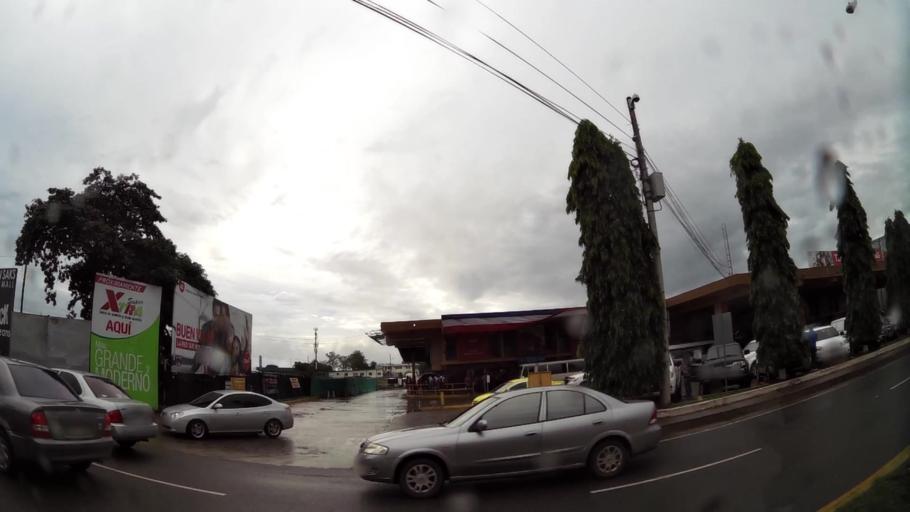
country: PA
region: Veraguas
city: Santiago de Veraguas
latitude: 8.1044
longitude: -80.9737
